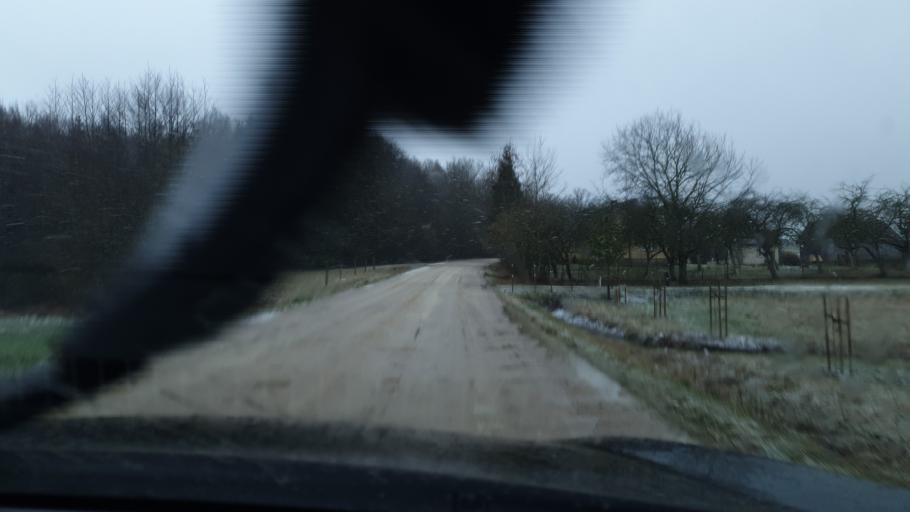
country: LT
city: Jieznas
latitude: 54.5688
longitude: 24.3184
